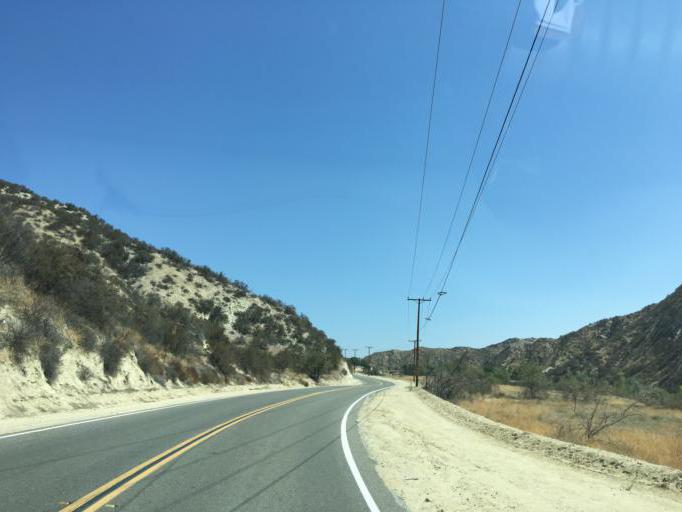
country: US
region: California
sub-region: Los Angeles County
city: Val Verde
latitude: 34.4344
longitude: -118.6596
